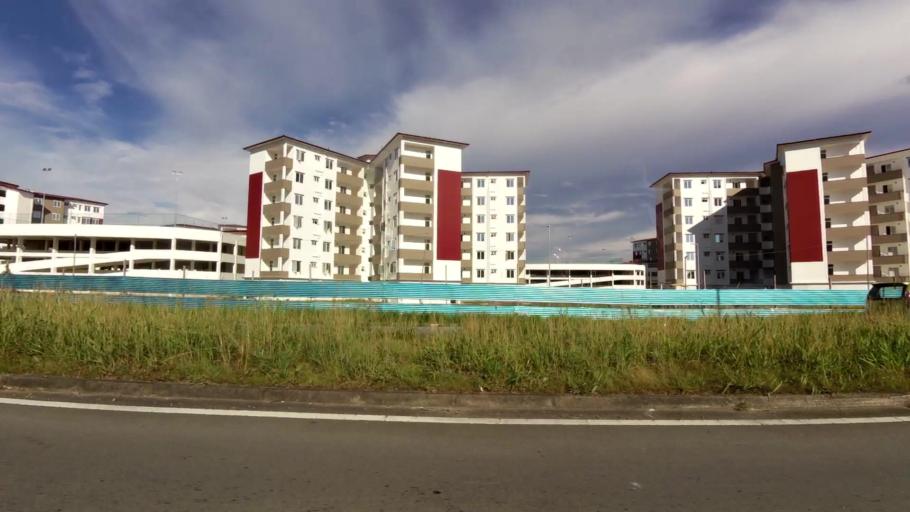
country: BN
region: Brunei and Muara
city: Bandar Seri Begawan
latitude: 4.9743
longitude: 114.9734
